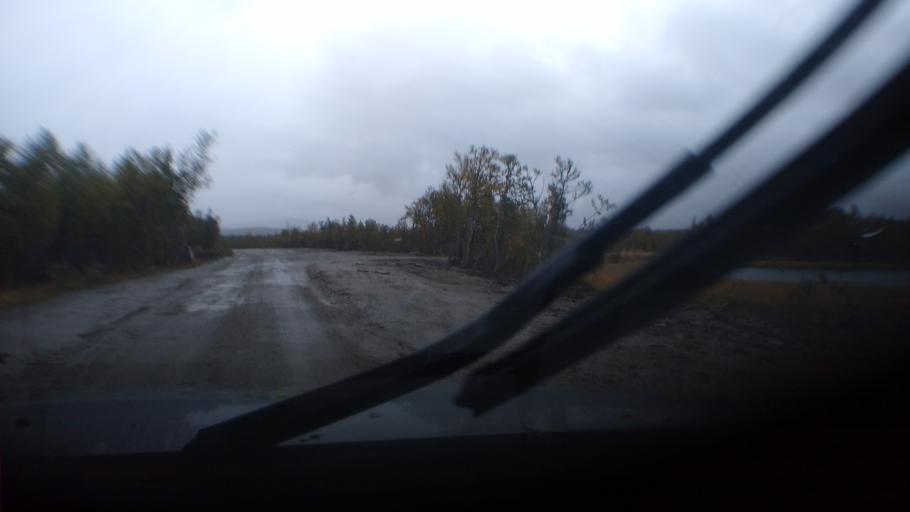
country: NO
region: Oppland
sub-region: Ringebu
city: Ringebu
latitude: 61.6541
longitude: 10.1021
